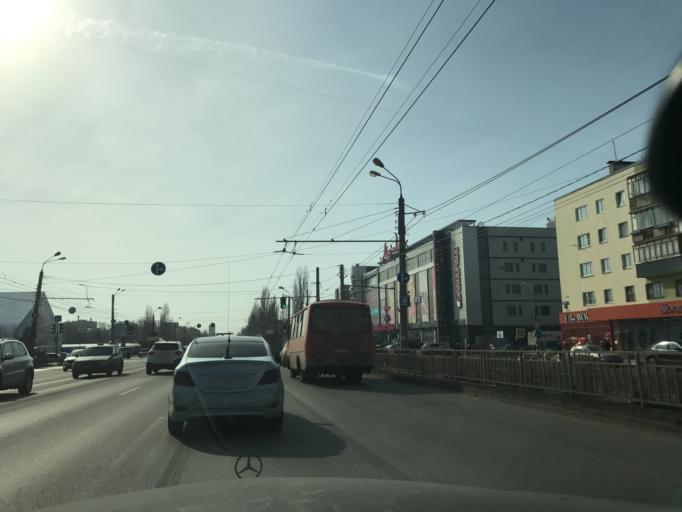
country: RU
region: Nizjnij Novgorod
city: Nizhniy Novgorod
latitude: 56.2884
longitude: 43.9302
